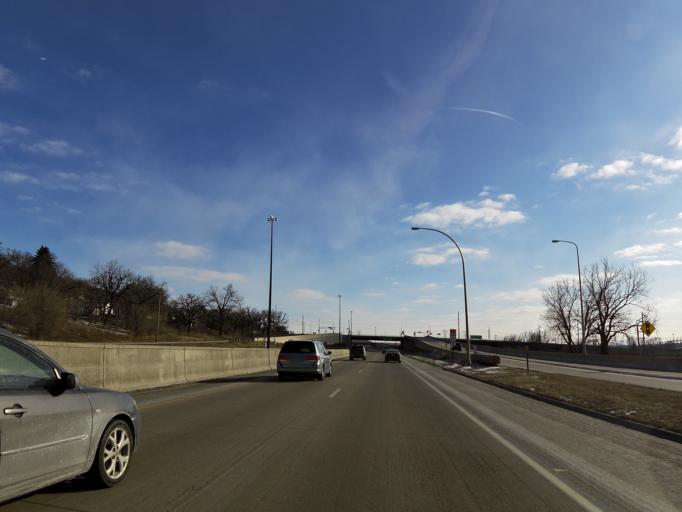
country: US
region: Minnesota
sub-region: Dakota County
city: South Saint Paul
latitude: 44.8949
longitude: -93.0084
